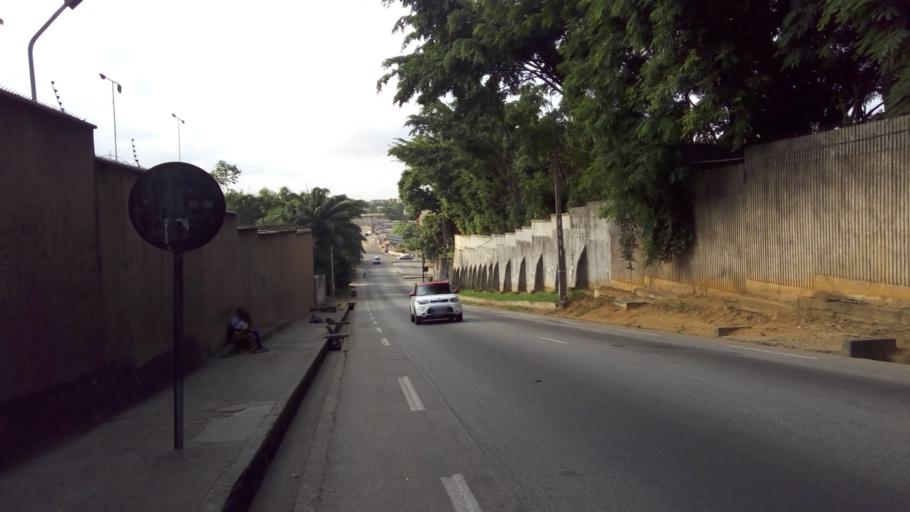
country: CI
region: Lagunes
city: Abidjan
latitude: 5.3397
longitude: -4.0217
